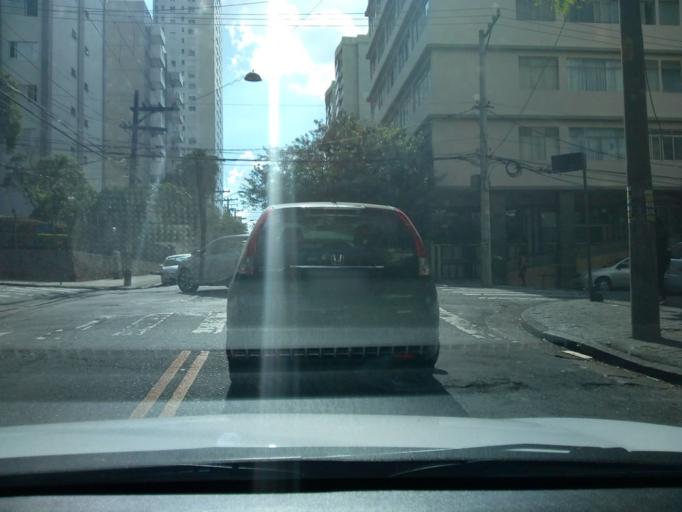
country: BR
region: Sao Paulo
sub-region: Sao Paulo
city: Sao Paulo
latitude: -23.5703
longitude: -46.6343
